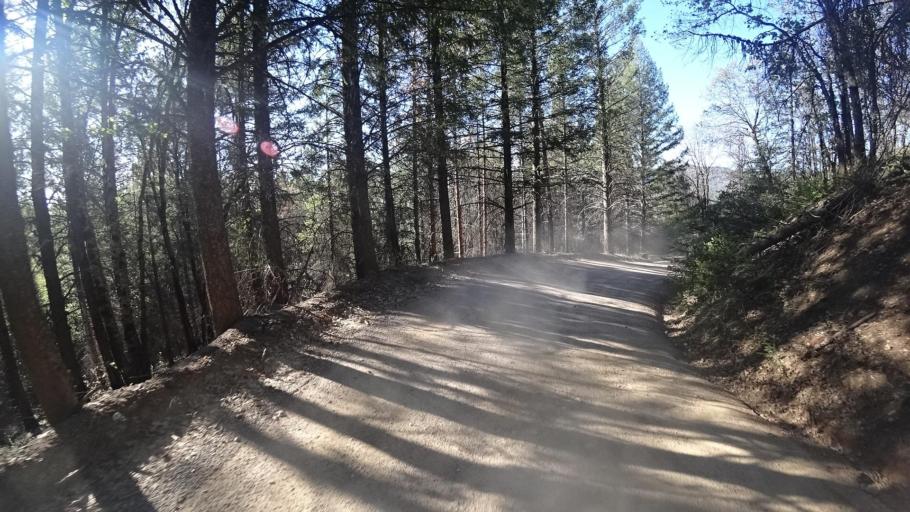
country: US
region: California
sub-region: Lake County
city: Upper Lake
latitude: 39.3462
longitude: -122.9692
